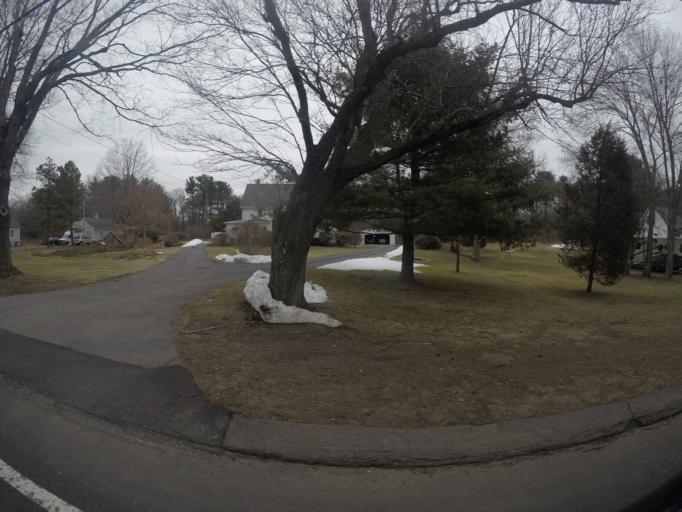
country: US
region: Massachusetts
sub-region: Bristol County
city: Easton
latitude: 42.0409
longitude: -71.0723
